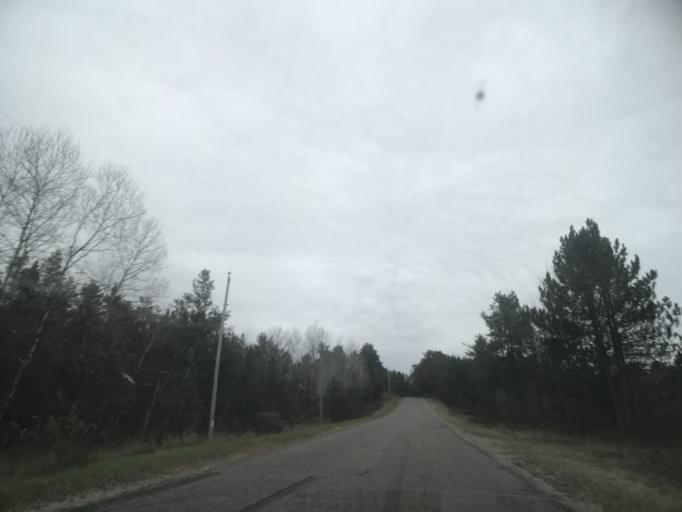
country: US
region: Wisconsin
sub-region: Oconto County
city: Gillett
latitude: 45.2734
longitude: -88.2571
